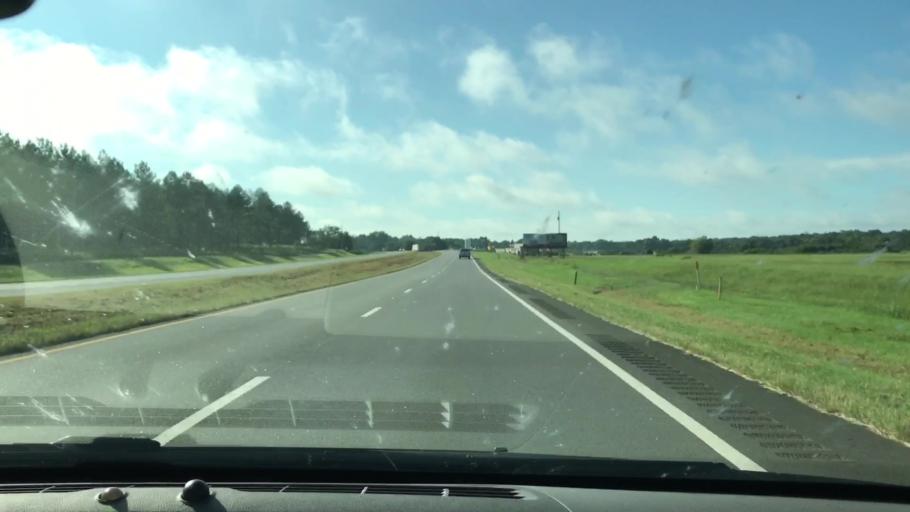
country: US
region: Georgia
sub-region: Terrell County
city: Dawson
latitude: 31.7471
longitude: -84.4185
